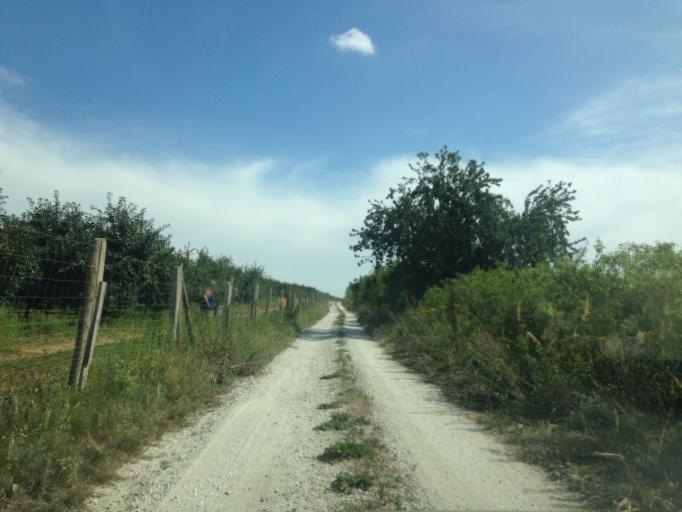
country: PL
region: Kujawsko-Pomorskie
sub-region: Powiat brodnicki
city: Bartniczka
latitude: 53.2355
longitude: 19.5781
